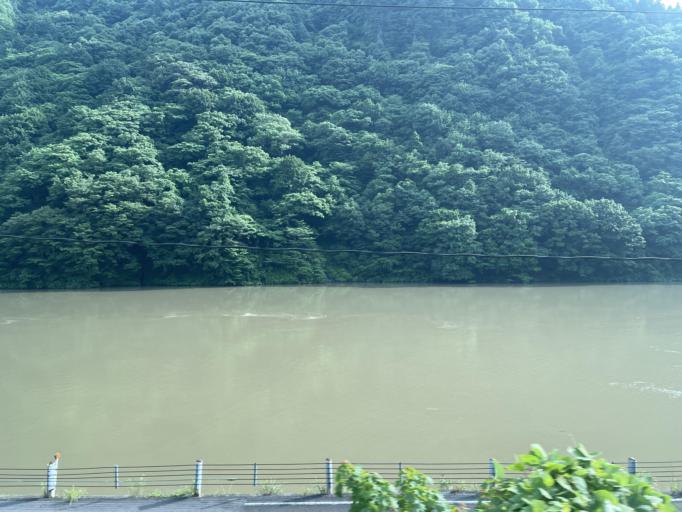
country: JP
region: Niigata
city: Suibara
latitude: 37.6985
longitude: 139.4119
